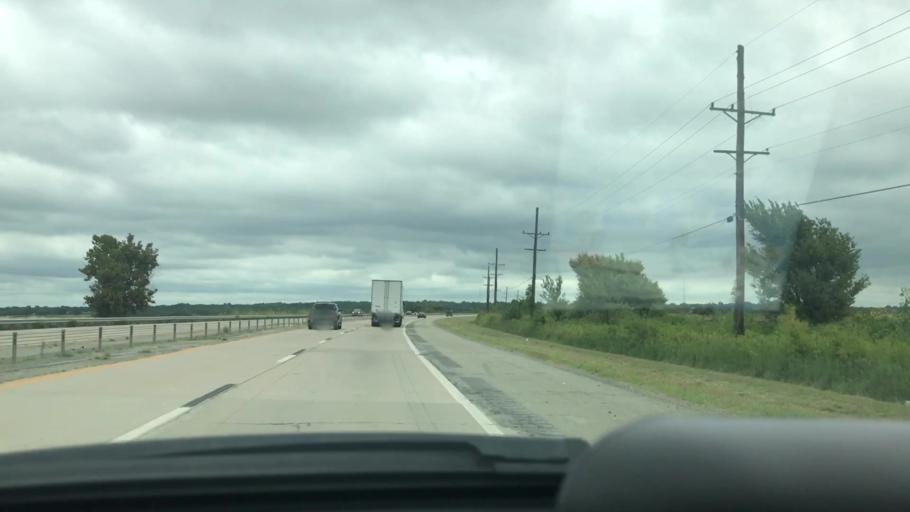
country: US
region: Oklahoma
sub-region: McIntosh County
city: Eufaula
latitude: 35.3375
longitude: -95.5863
